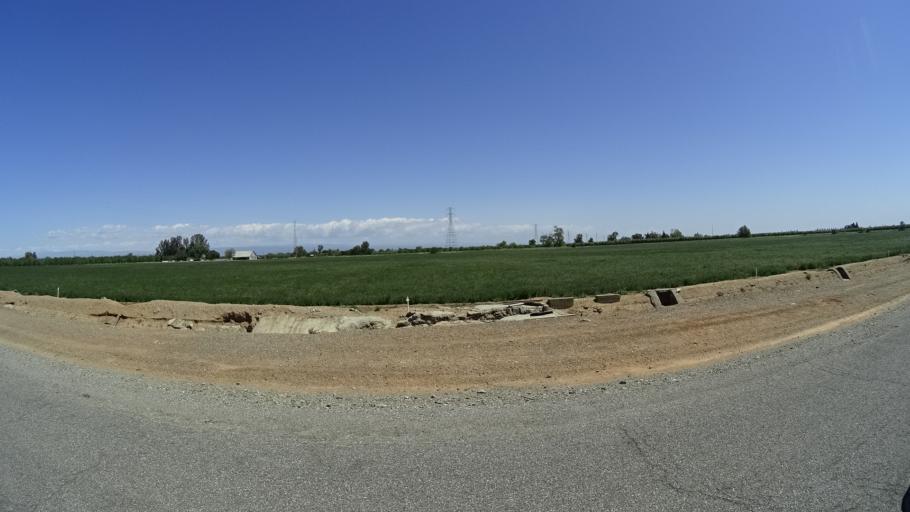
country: US
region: California
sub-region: Glenn County
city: Orland
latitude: 39.7954
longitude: -122.1785
